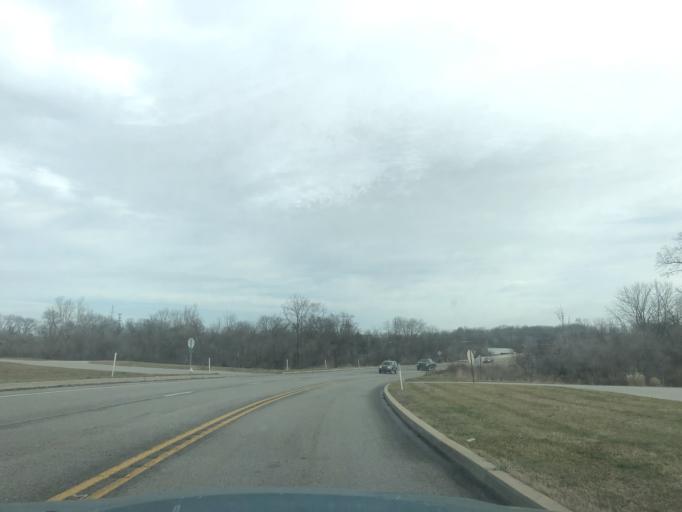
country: US
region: Pennsylvania
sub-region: Montgomery County
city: Kulpsville
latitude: 40.2569
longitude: -75.3582
